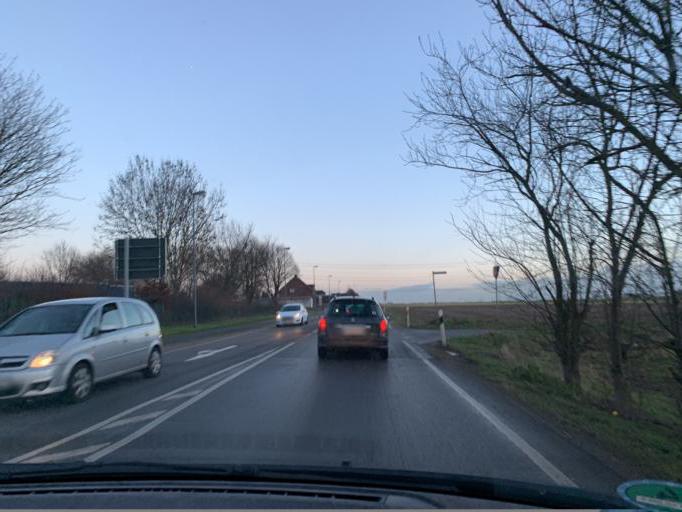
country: DE
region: North Rhine-Westphalia
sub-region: Regierungsbezirk Dusseldorf
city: Grevenbroich
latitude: 51.0674
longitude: 6.6325
